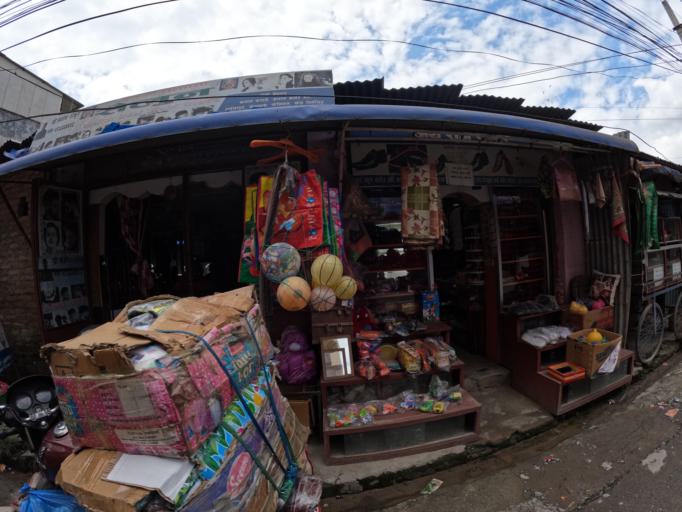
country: NP
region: Central Region
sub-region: Bagmati Zone
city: Kathmandu
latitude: 27.7498
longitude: 85.3161
